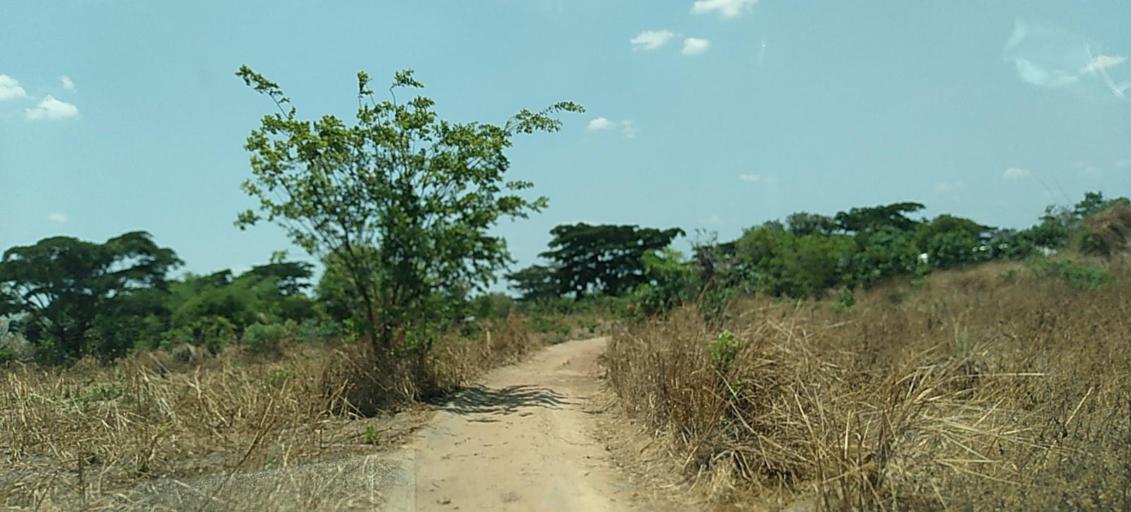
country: ZM
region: Copperbelt
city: Luanshya
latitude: -13.0687
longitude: 28.4061
